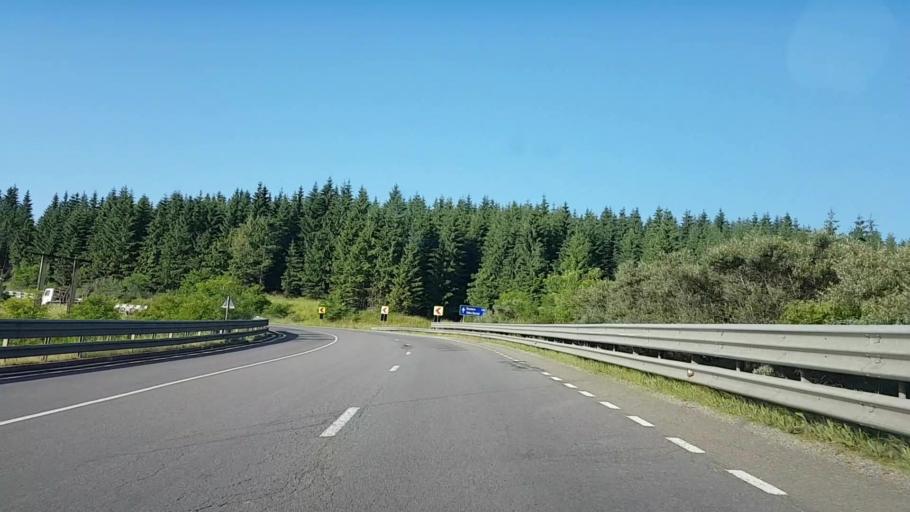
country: RO
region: Bistrita-Nasaud
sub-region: Comuna Lunca Ilvei
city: Lunca Ilvei
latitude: 47.2402
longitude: 25.0183
